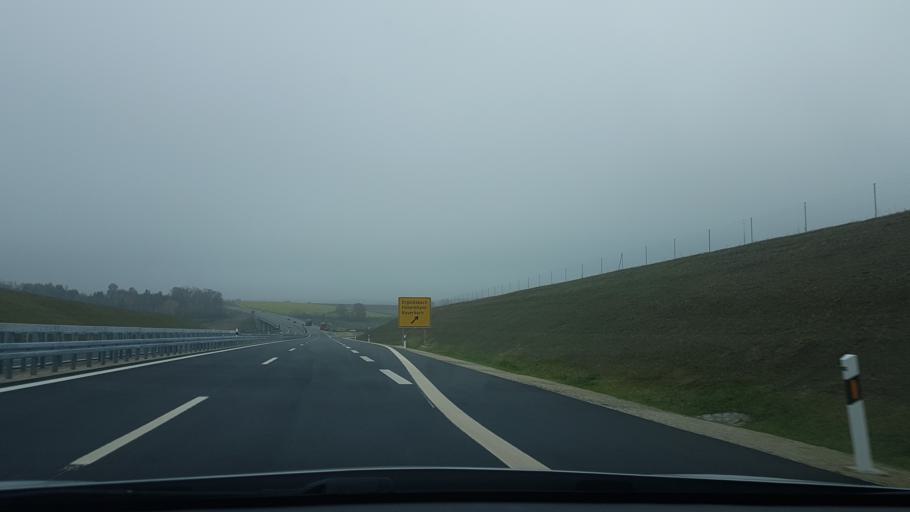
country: DE
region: Bavaria
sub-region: Lower Bavaria
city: Ergoldsbach
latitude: 48.6667
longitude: 12.1899
